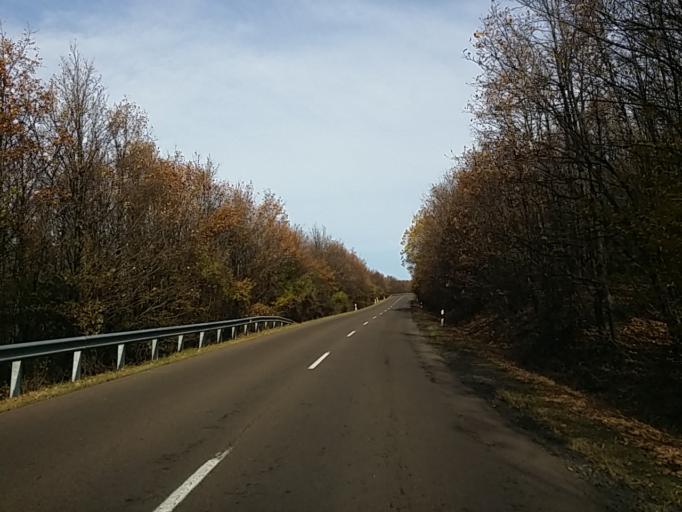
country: HU
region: Heves
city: Gyongyossolymos
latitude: 47.8569
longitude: 19.9685
